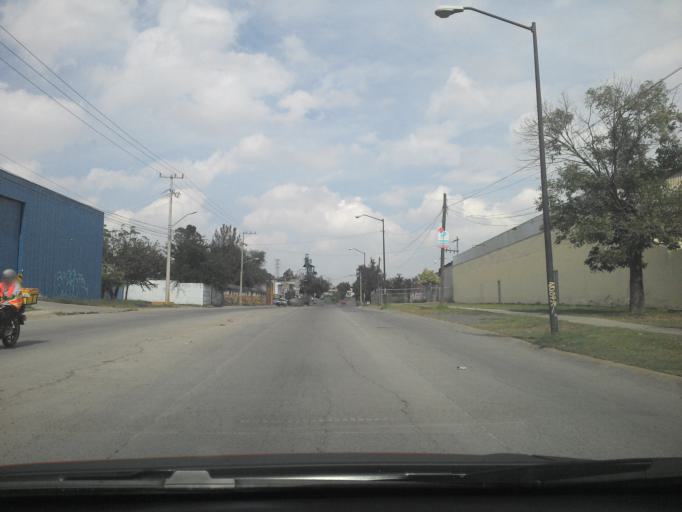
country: MX
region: Jalisco
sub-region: Tlajomulco de Zuniga
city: Altus Bosques
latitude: 20.5859
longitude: -103.3529
